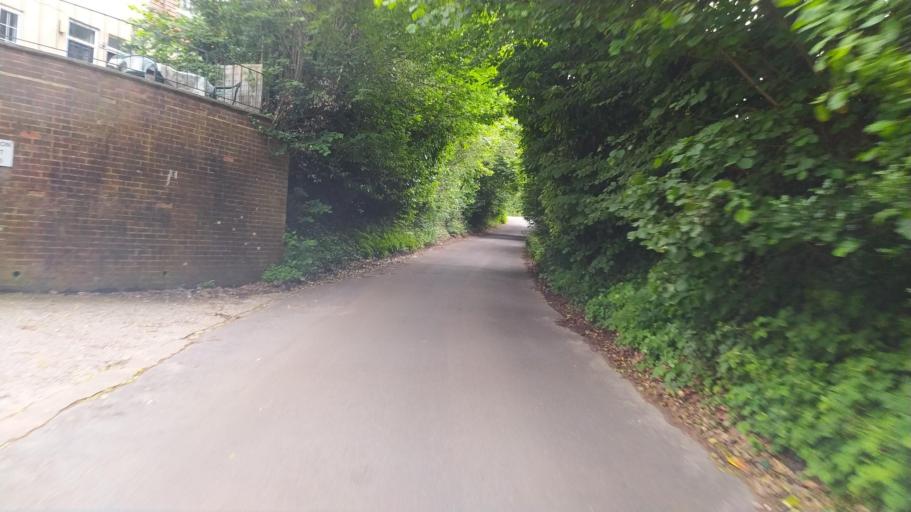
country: GB
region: England
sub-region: Hampshire
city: Liphook
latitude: 51.0861
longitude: -0.8059
